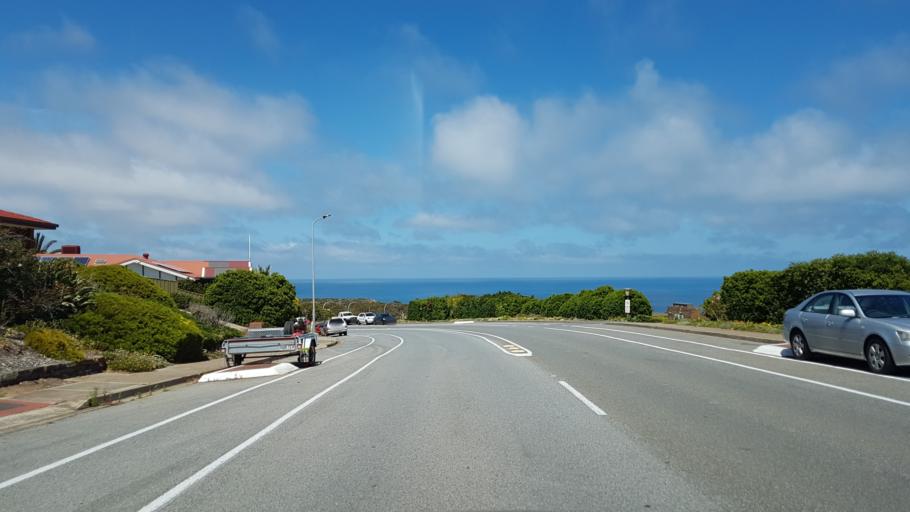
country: AU
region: South Australia
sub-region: Marion
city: Marino
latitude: -35.0664
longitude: 138.5073
